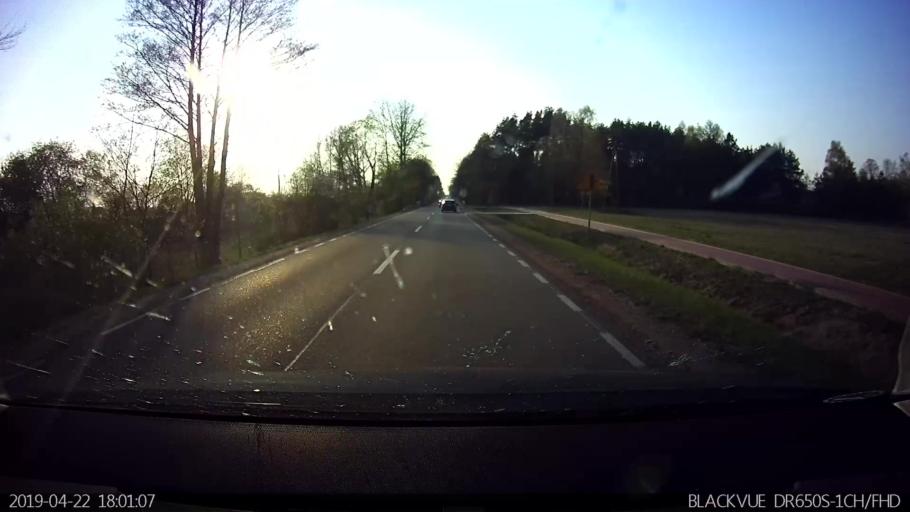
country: PL
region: Masovian Voivodeship
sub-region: Powiat wegrowski
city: Korytnica
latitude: 52.4776
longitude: 21.8353
